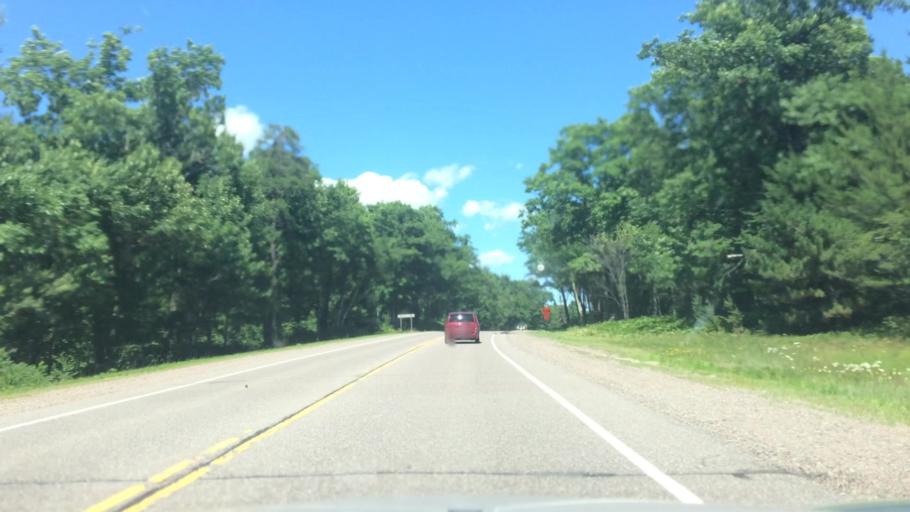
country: US
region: Wisconsin
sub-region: Vilas County
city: Lac du Flambeau
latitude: 45.7790
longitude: -89.7147
